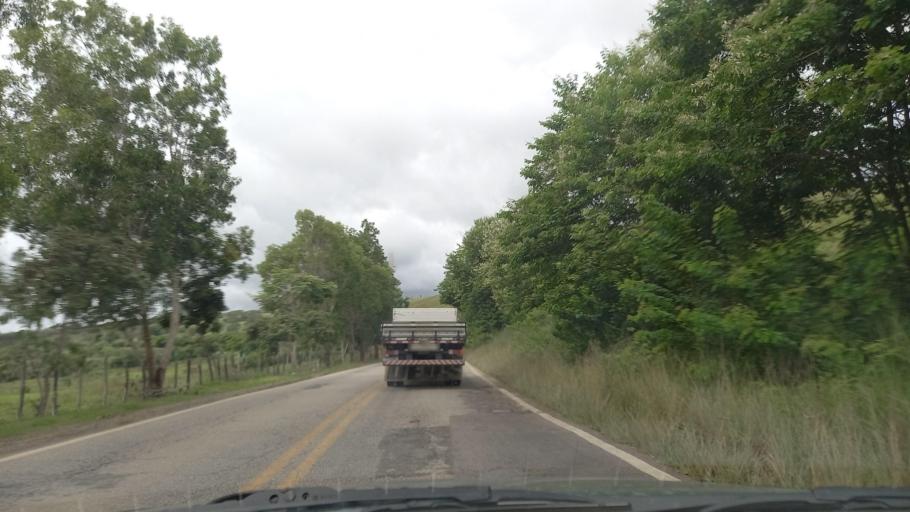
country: BR
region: Pernambuco
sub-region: Canhotinho
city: Canhotinho
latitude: -8.8656
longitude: -36.1883
